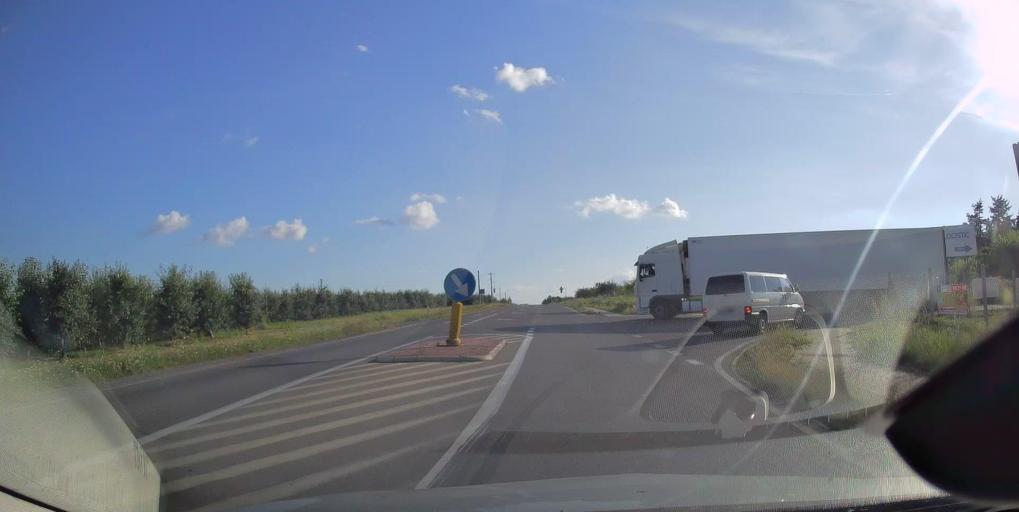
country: PL
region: Masovian Voivodeship
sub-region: Powiat grojecki
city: Belsk Duzy
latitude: 51.8407
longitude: 20.8285
